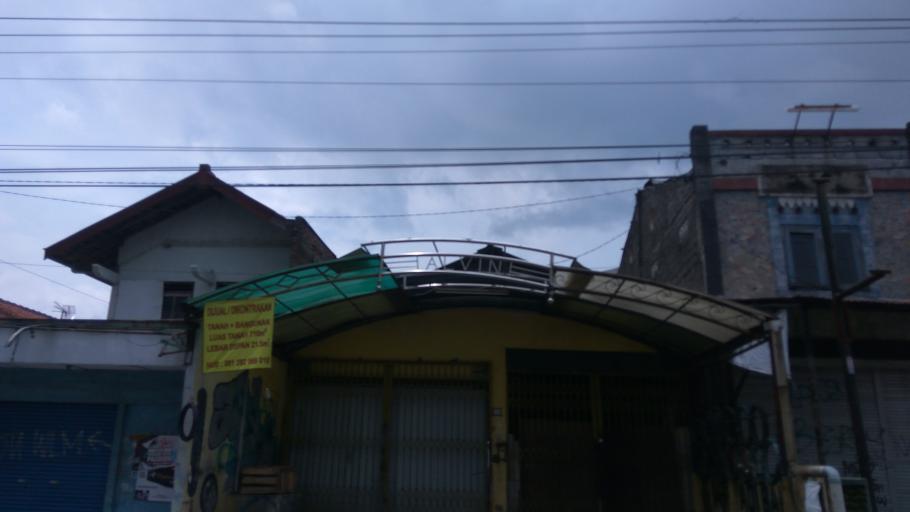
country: ID
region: Daerah Istimewa Yogyakarta
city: Melati
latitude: -7.7314
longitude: 110.3788
